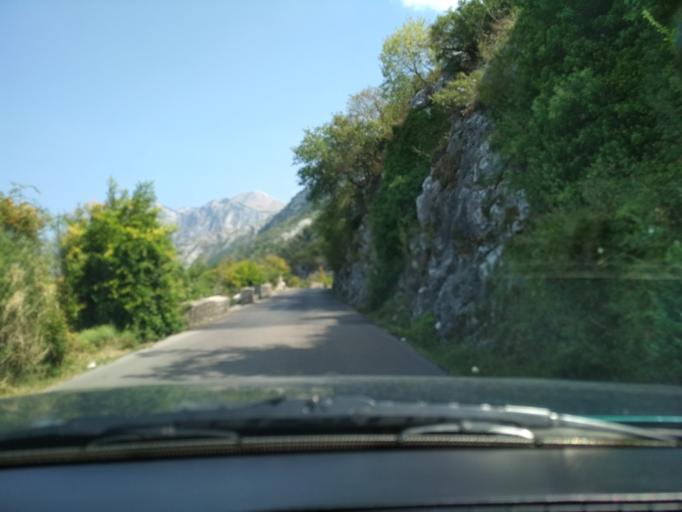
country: ME
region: Kotor
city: Kotor
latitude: 42.3999
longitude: 18.7724
